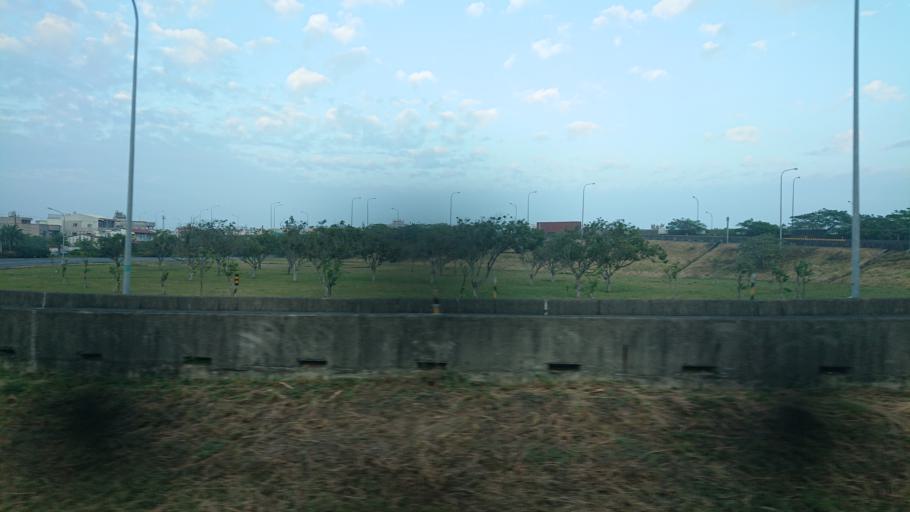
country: TW
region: Taiwan
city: Xinying
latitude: 23.1806
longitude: 120.2338
